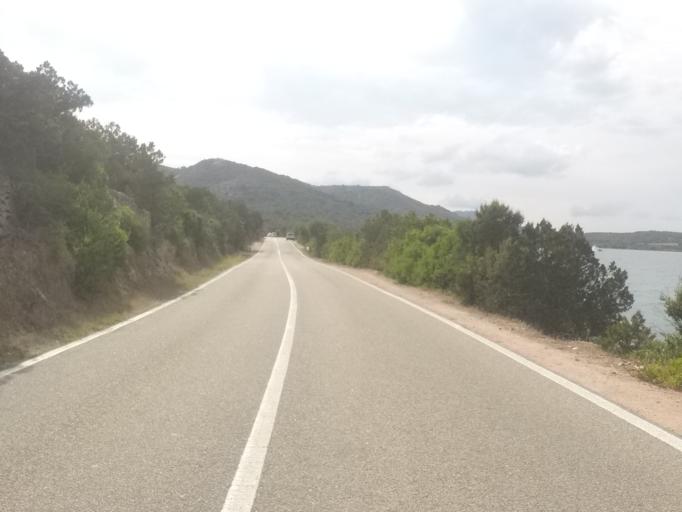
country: IT
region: Sardinia
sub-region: Provincia di Olbia-Tempio
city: Palau
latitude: 41.1560
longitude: 9.4143
